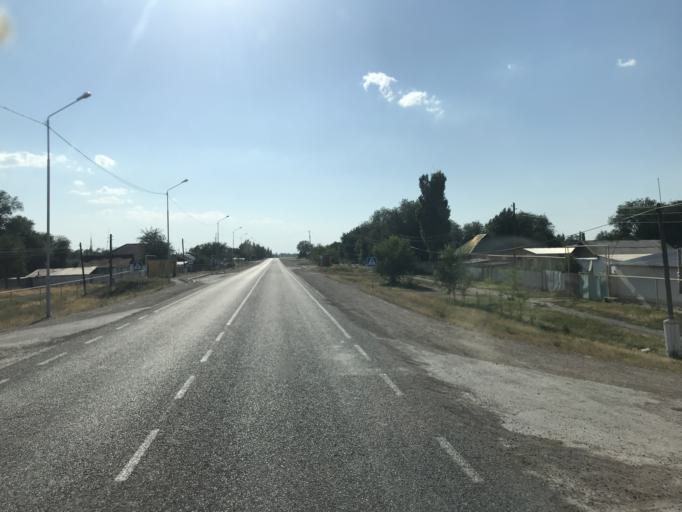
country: KZ
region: Zhambyl
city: Georgiyevka
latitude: 43.2275
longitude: 74.3927
